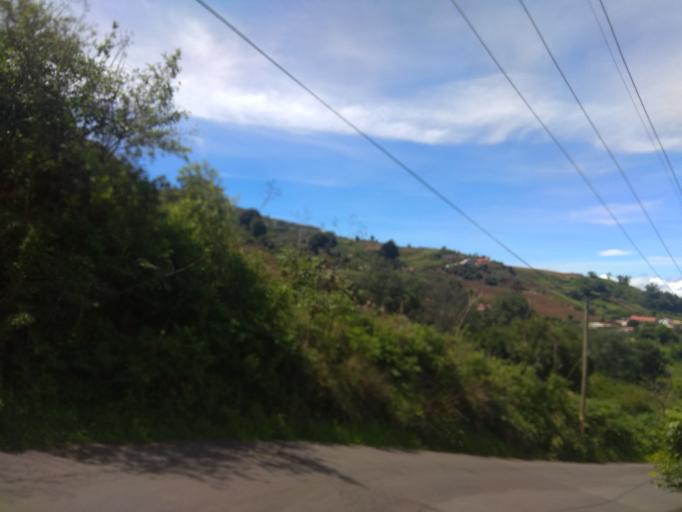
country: CR
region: Cartago
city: Cot
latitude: 9.9261
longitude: -83.8999
